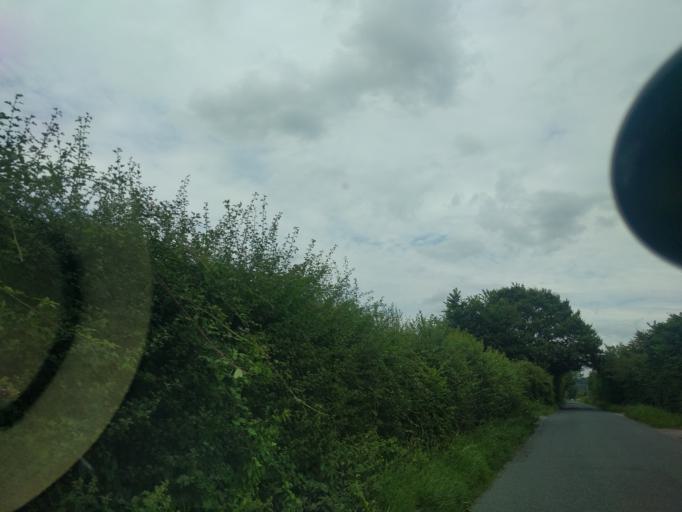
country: GB
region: England
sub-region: Wiltshire
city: Lacock
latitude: 51.3898
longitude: -2.1111
